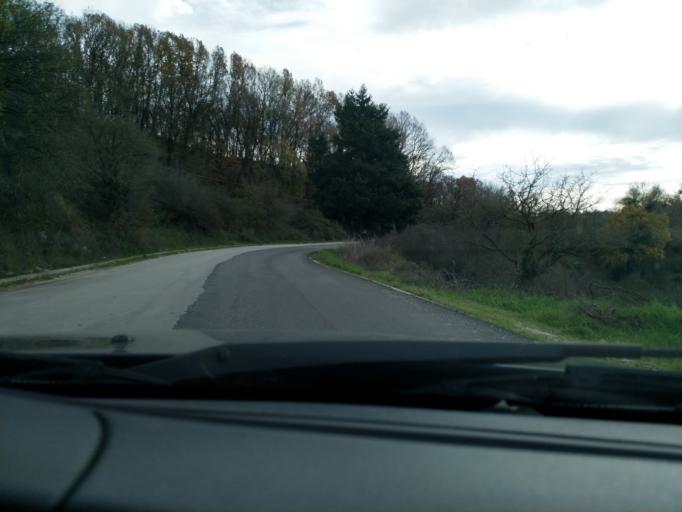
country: GR
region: Epirus
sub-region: Nomos Prevezis
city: Filippiada
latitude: 39.2168
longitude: 20.8599
